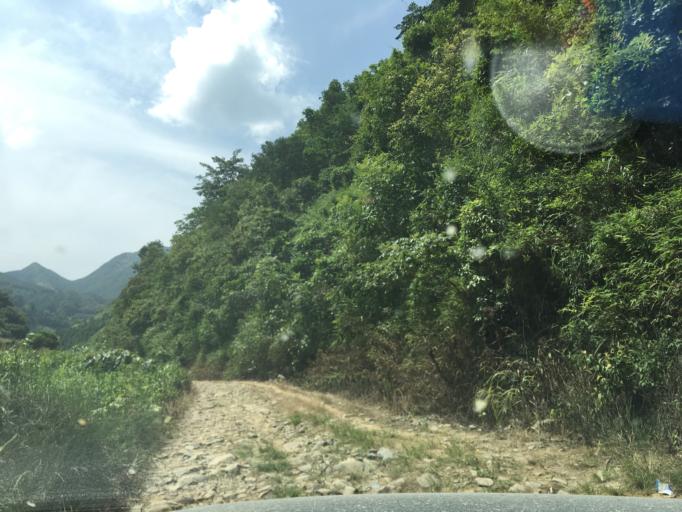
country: CN
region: Guangxi Zhuangzu Zizhiqu
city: Xinzhou
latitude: 24.9535
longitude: 105.7933
